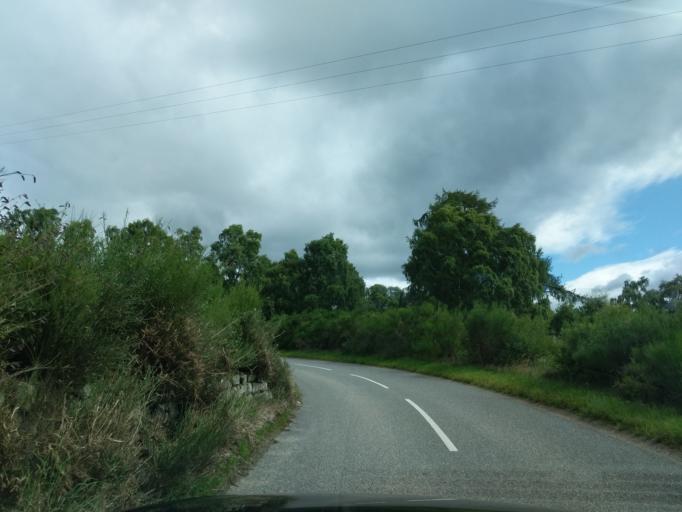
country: GB
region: Scotland
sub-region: Aberdeenshire
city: Ballater
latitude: 57.0596
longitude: -2.9640
